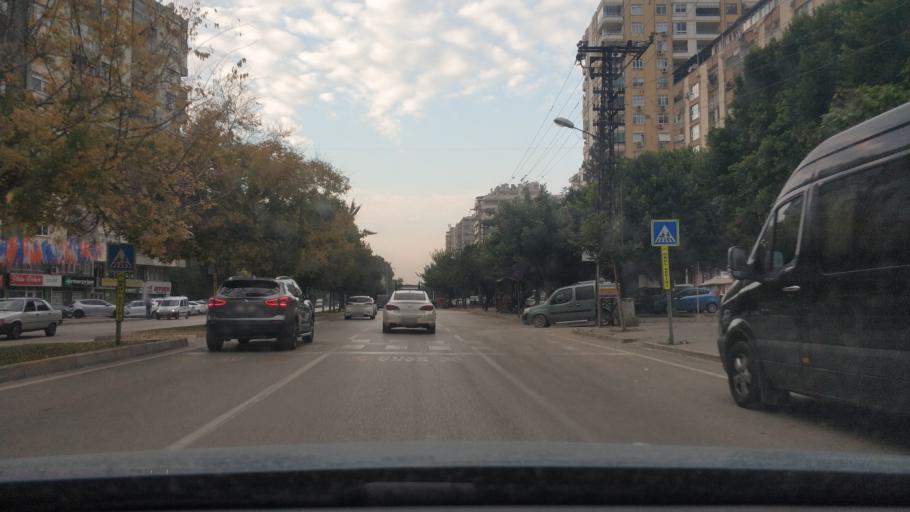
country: TR
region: Adana
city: Adana
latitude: 36.9985
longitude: 35.3175
